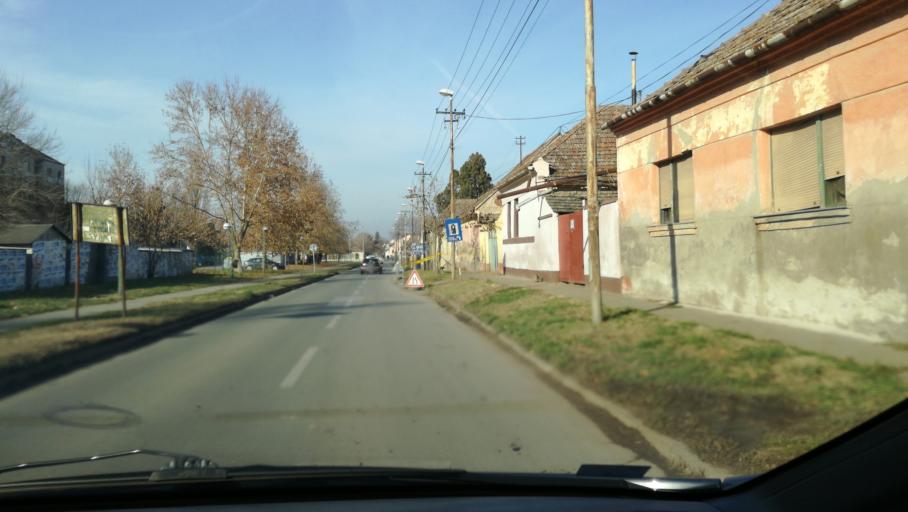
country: RS
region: Autonomna Pokrajina Vojvodina
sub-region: Severnobanatski Okrug
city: Kikinda
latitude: 45.8182
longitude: 20.4503
